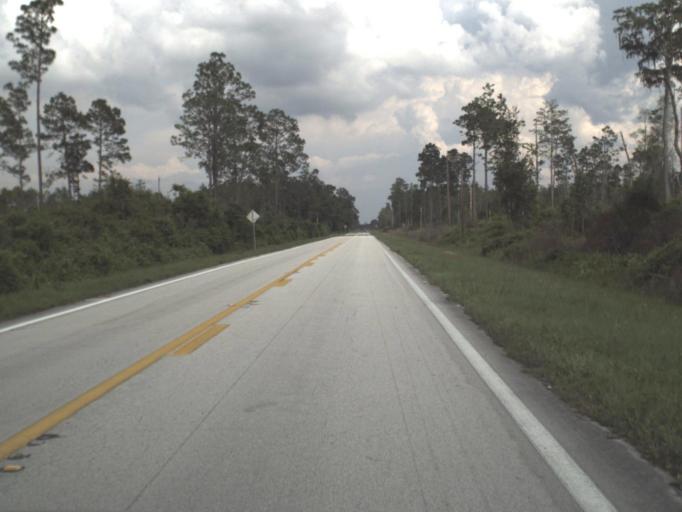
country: US
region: Florida
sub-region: Baker County
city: Macclenny
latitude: 30.5209
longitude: -82.2877
